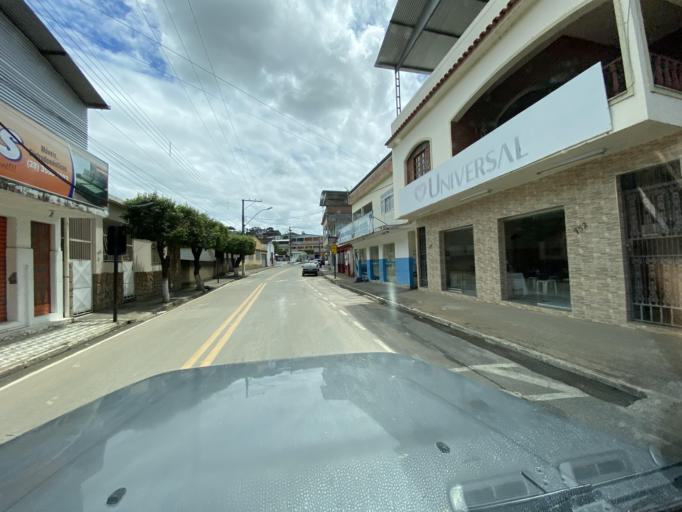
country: BR
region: Espirito Santo
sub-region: Jeronimo Monteiro
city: Jeronimo Monteiro
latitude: -20.7914
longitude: -41.3985
